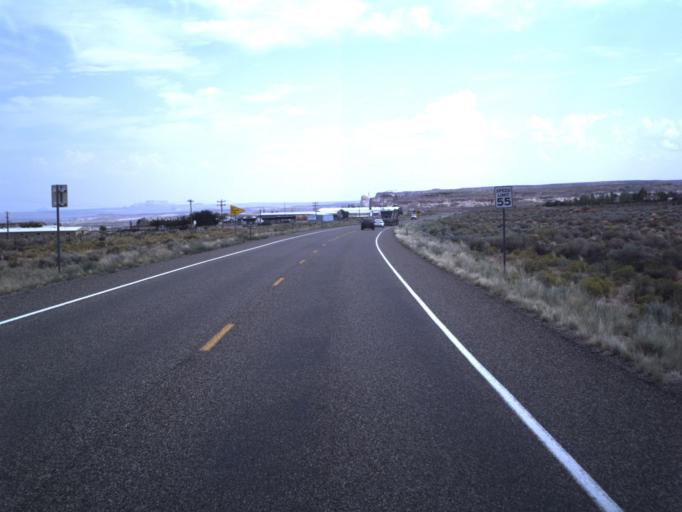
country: US
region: Arizona
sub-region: Coconino County
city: Page
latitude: 37.0719
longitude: -111.6516
